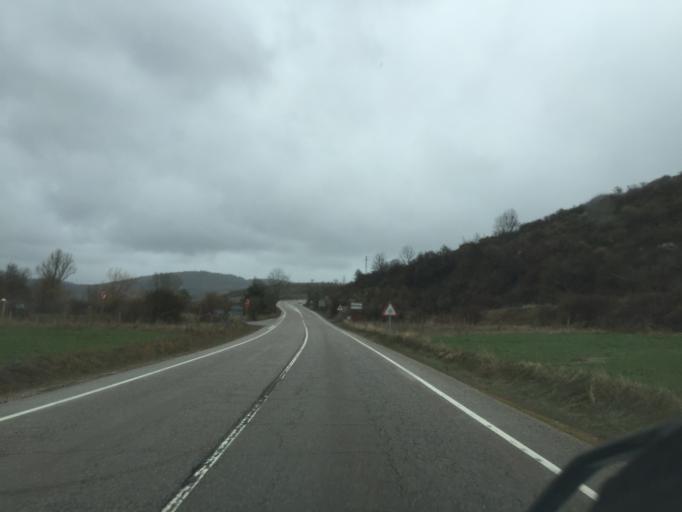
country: ES
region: Castille and Leon
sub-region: Provincia de Leon
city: Carrocera
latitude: 42.7854
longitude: -5.7620
